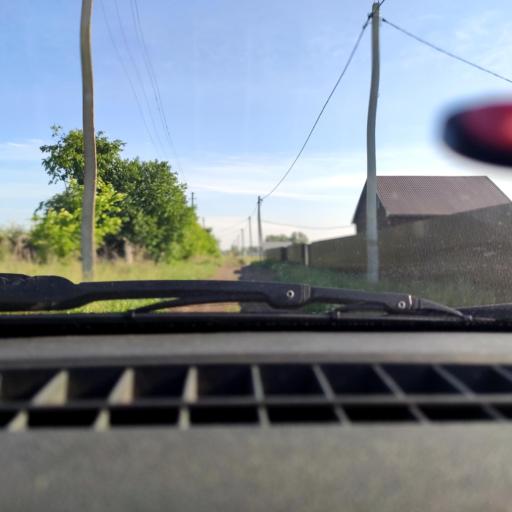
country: RU
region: Bashkortostan
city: Avdon
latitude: 54.4626
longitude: 55.8192
